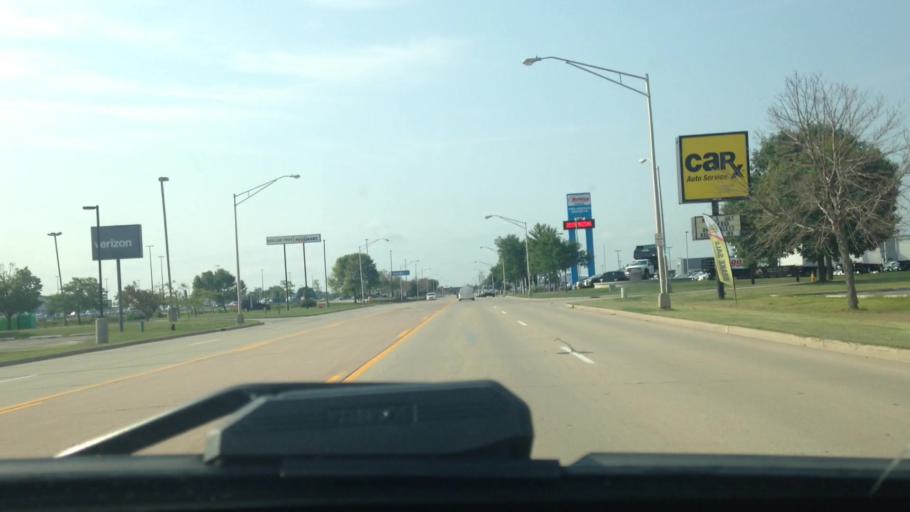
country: US
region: Wisconsin
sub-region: Fond du Lac County
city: North Fond du Lac
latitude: 43.7905
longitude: -88.4866
